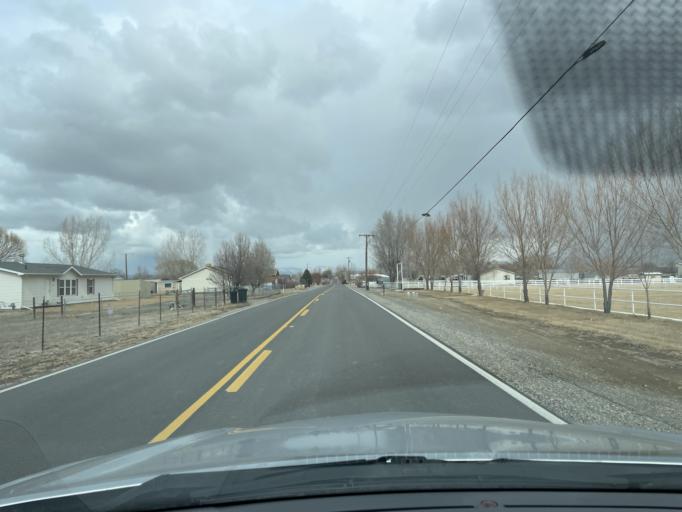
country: US
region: Colorado
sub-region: Mesa County
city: Loma
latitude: 39.1971
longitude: -108.8083
